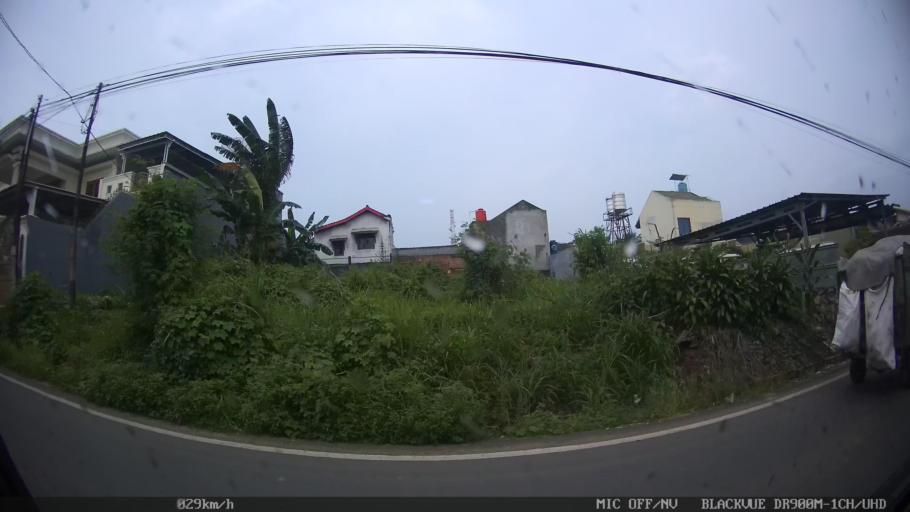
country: ID
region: Lampung
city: Kedaton
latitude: -5.3979
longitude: 105.2780
